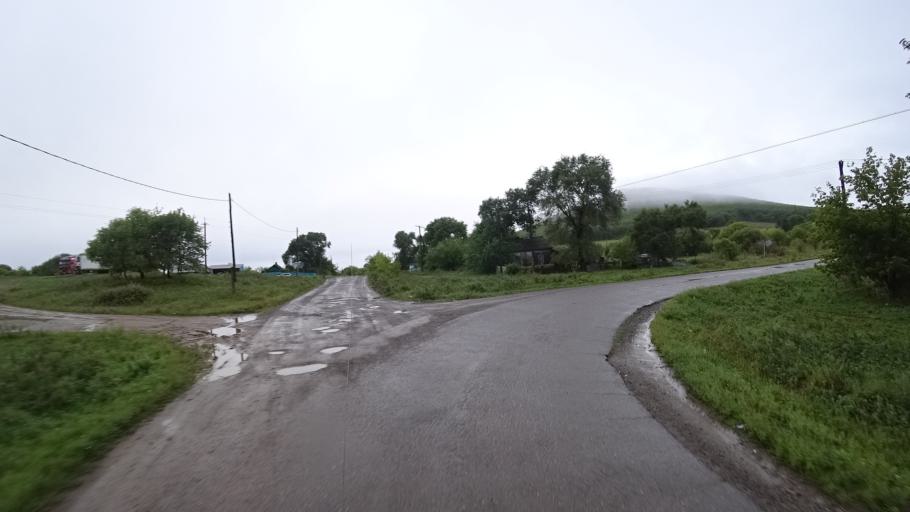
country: RU
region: Primorskiy
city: Monastyrishche
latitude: 44.2571
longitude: 132.4194
